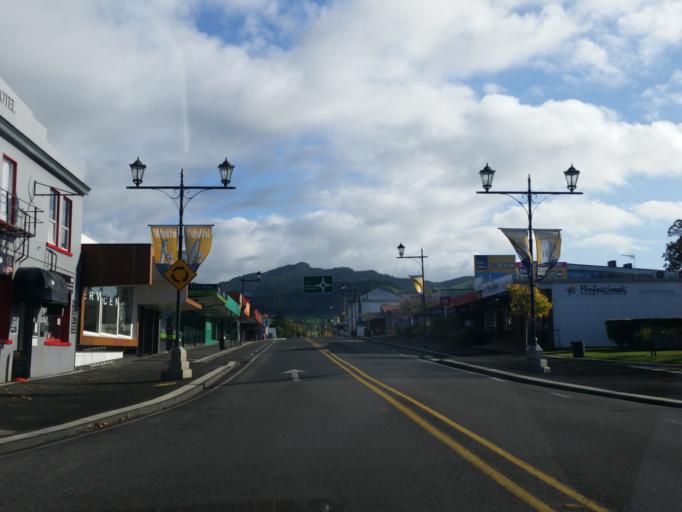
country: NZ
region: Waikato
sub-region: Hauraki District
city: Waihi
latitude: -37.3927
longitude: 175.8414
